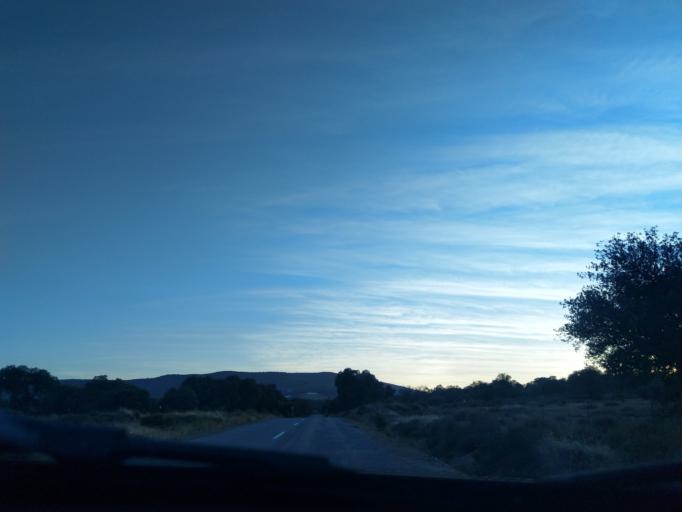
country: ES
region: Extremadura
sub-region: Provincia de Badajoz
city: Valverde de Llerena
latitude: 38.1754
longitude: -5.8721
